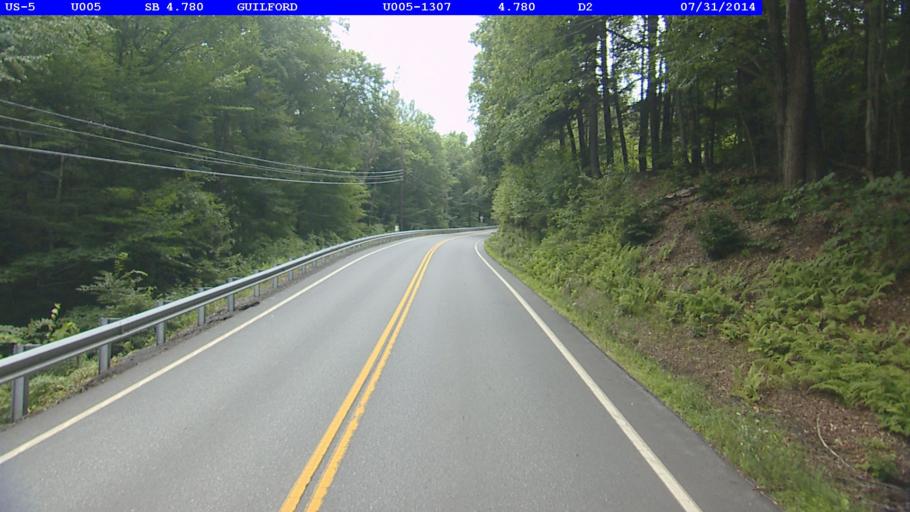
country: US
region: Vermont
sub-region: Windham County
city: Brattleboro
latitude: 42.7964
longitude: -72.5637
